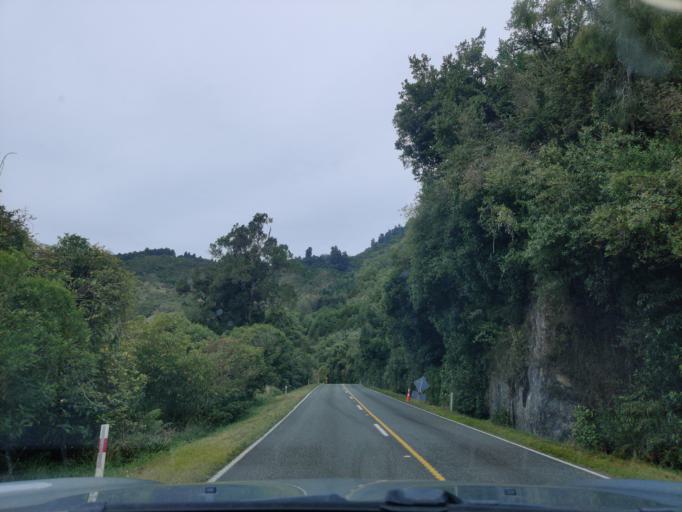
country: NZ
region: West Coast
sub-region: Buller District
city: Westport
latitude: -41.8439
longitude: 171.9098
